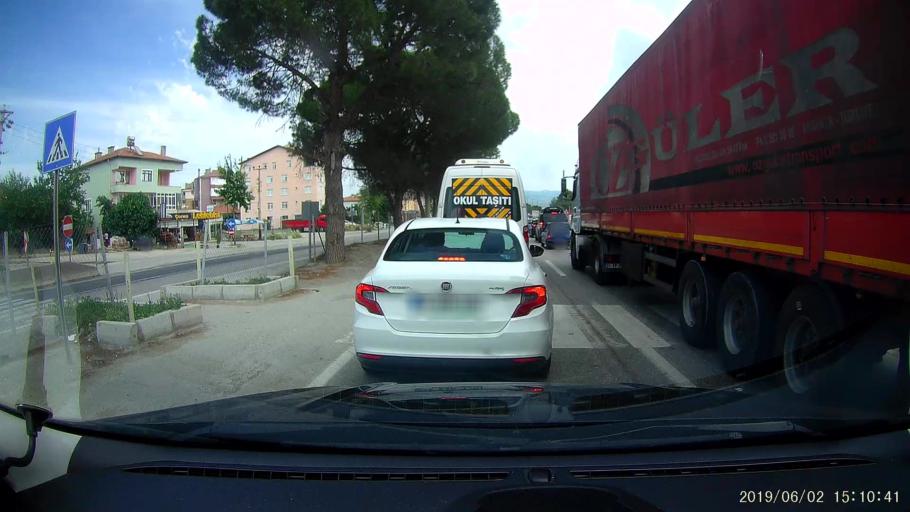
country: TR
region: Corum
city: Osmancik
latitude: 40.9786
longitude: 34.8062
